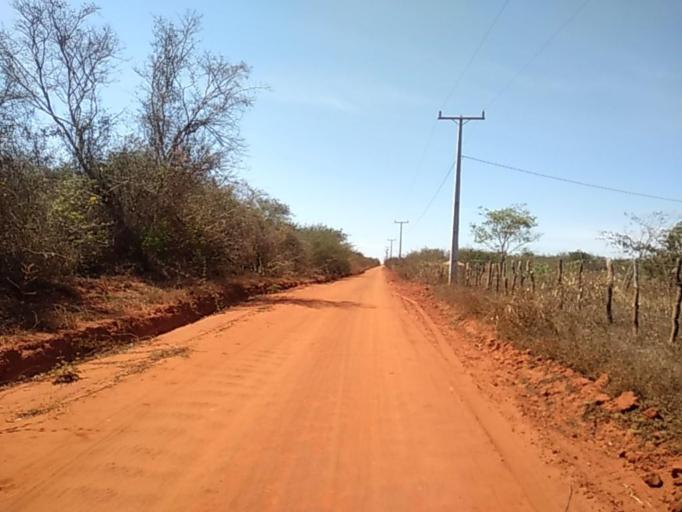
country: BR
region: Bahia
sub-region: Caetite
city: Caetite
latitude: -13.9833
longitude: -42.5105
